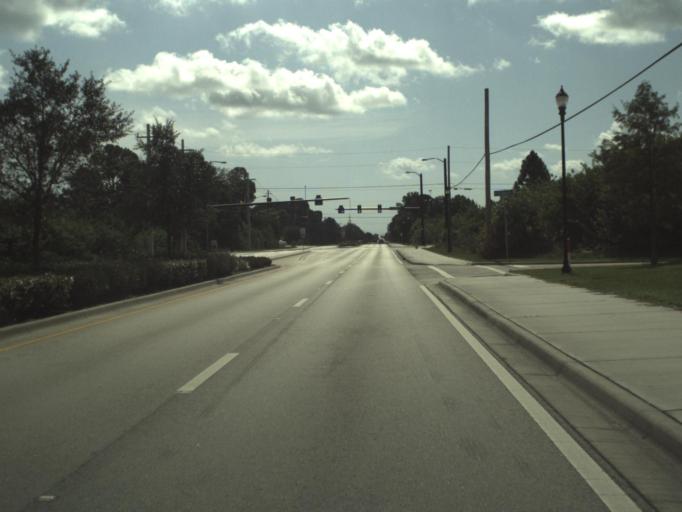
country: US
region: Florida
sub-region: Saint Lucie County
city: Port Saint Lucie
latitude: 27.2095
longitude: -80.3576
